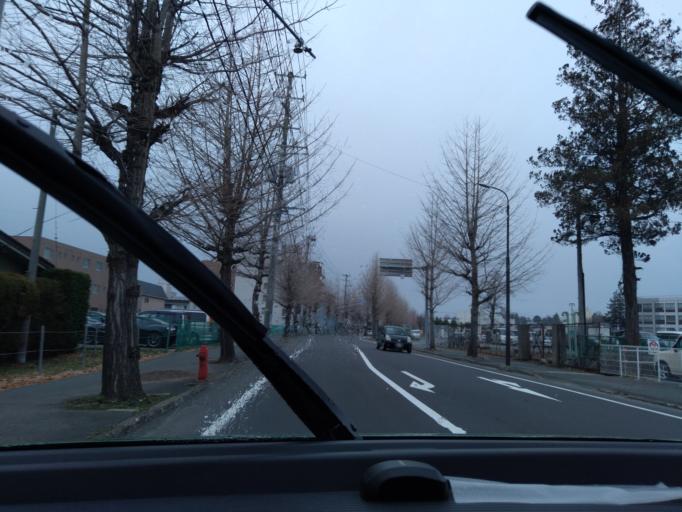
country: JP
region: Iwate
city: Morioka-shi
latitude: 39.7082
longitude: 141.1454
